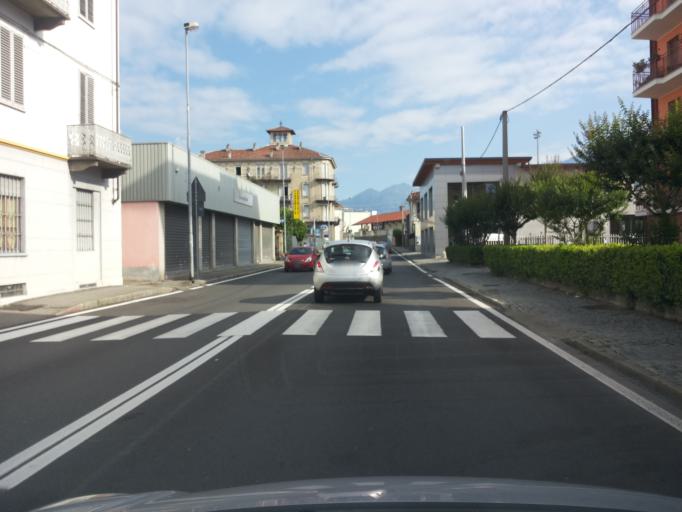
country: IT
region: Piedmont
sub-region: Provincia di Torino
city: Ivrea
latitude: 45.4589
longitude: 7.8780
